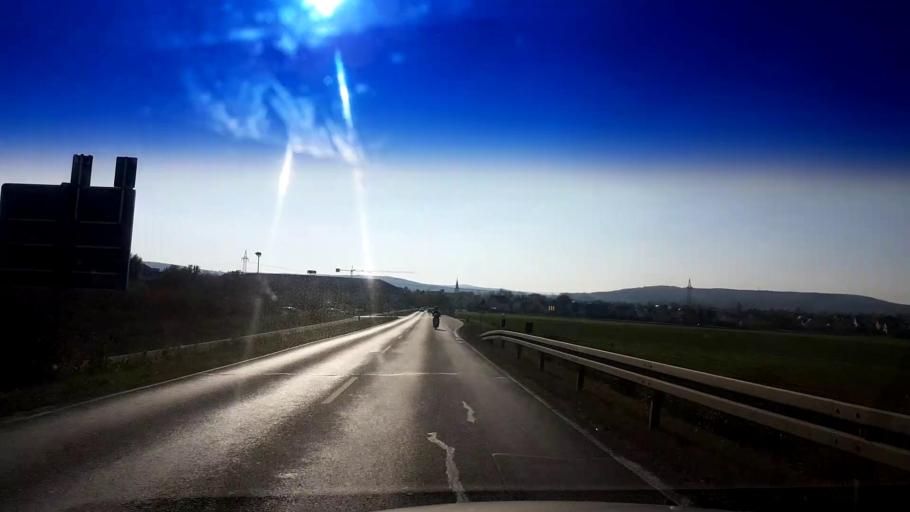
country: DE
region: Bavaria
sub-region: Upper Franconia
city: Hirschaid
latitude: 49.8231
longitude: 11.0048
